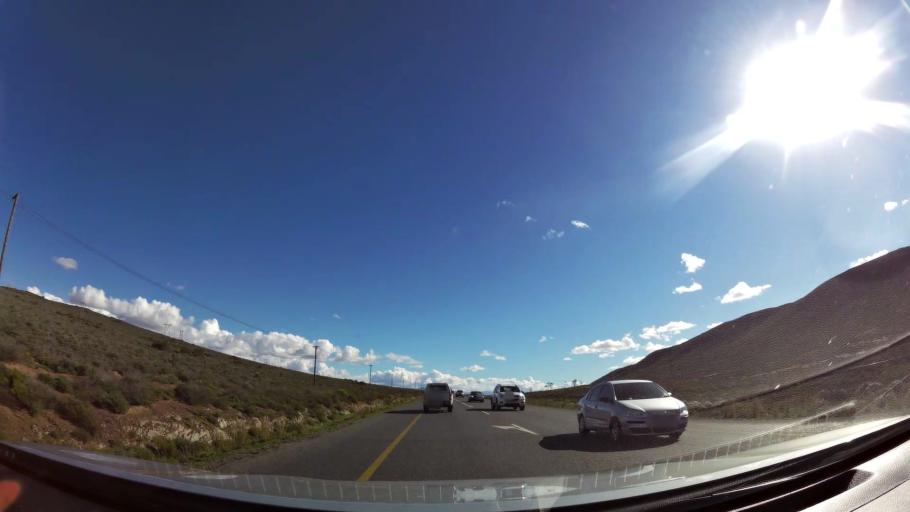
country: ZA
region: Western Cape
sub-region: Cape Winelands District Municipality
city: Worcester
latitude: -33.7349
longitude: 19.6613
